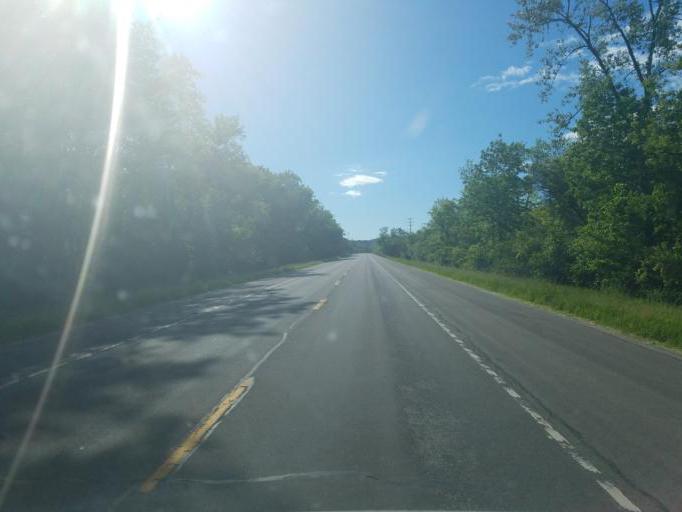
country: US
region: New York
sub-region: Herkimer County
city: Little Falls
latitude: 43.0317
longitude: -74.8264
